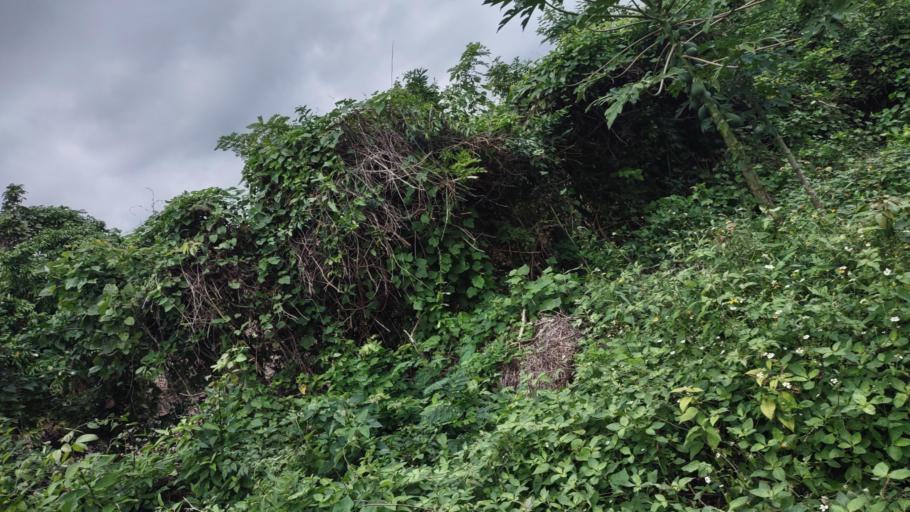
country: MX
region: Veracruz
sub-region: Coatzintla
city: Manuel Maria Contreras
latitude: 20.4130
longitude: -97.4580
